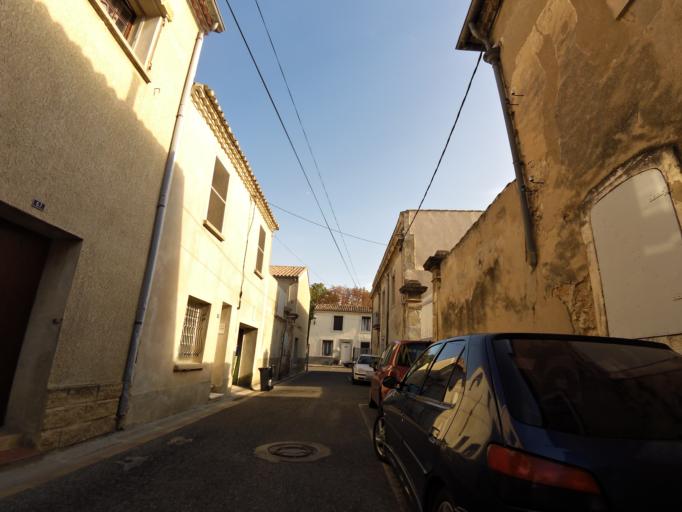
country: FR
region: Languedoc-Roussillon
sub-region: Departement de l'Herault
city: Lunel-Viel
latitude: 43.6786
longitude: 4.0918
